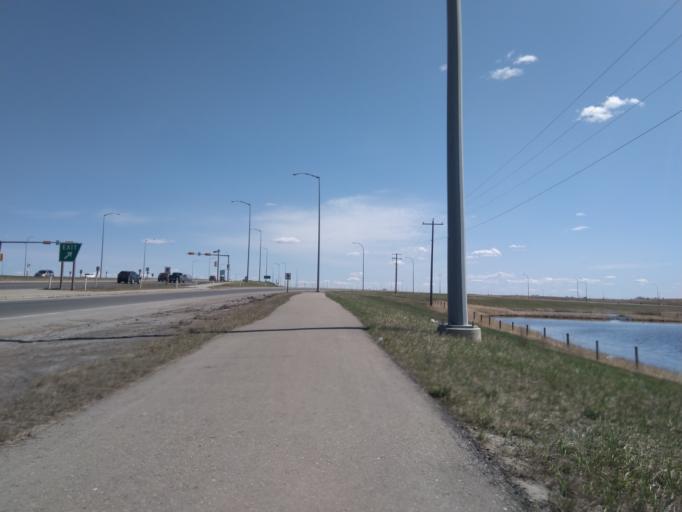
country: CA
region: Alberta
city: Chestermere
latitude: 51.0375
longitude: -113.9264
